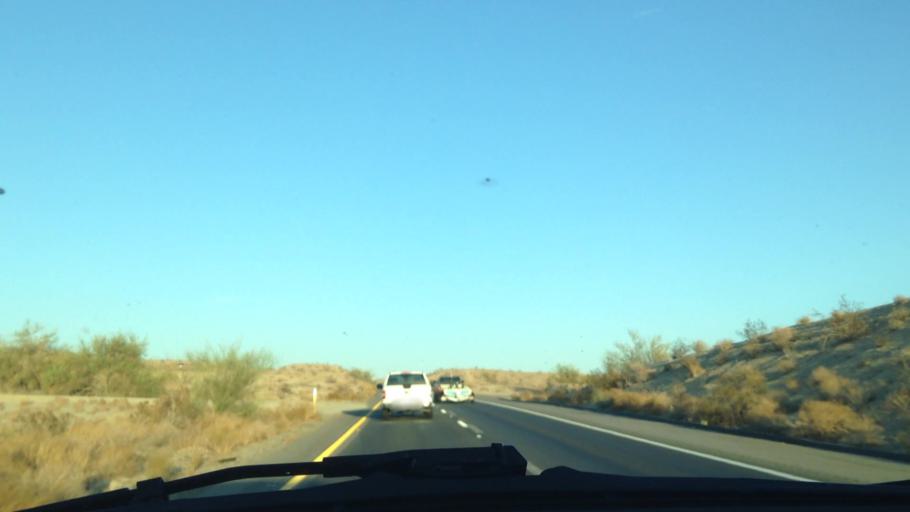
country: US
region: California
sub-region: Riverside County
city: Thermal
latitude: 33.6849
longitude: -116.0245
